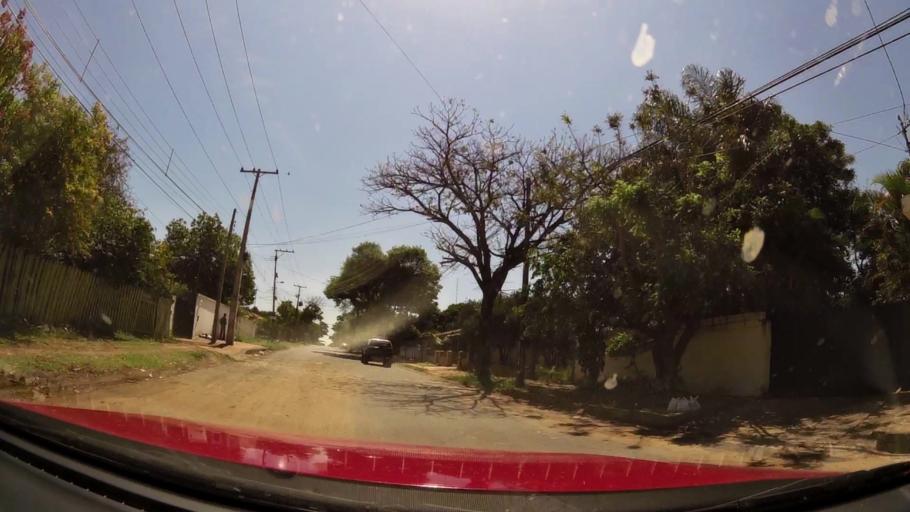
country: PY
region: Central
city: Colonia Mariano Roque Alonso
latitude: -25.2303
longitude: -57.5456
